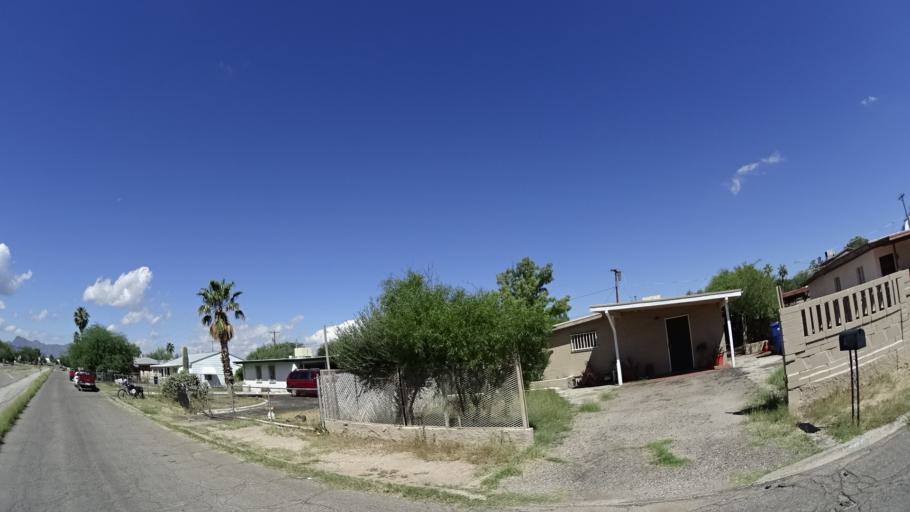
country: US
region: Arizona
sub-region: Pima County
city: Tucson
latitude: 32.2448
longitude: -110.9625
